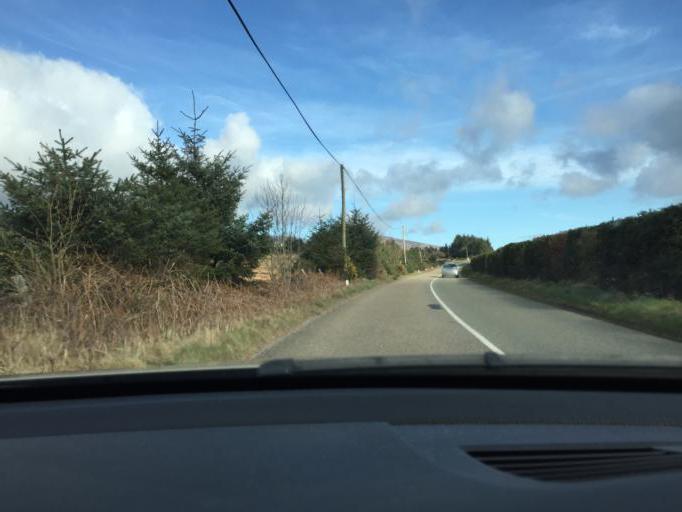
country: IE
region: Leinster
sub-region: Wicklow
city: Valleymount
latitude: 53.0613
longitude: -6.4877
